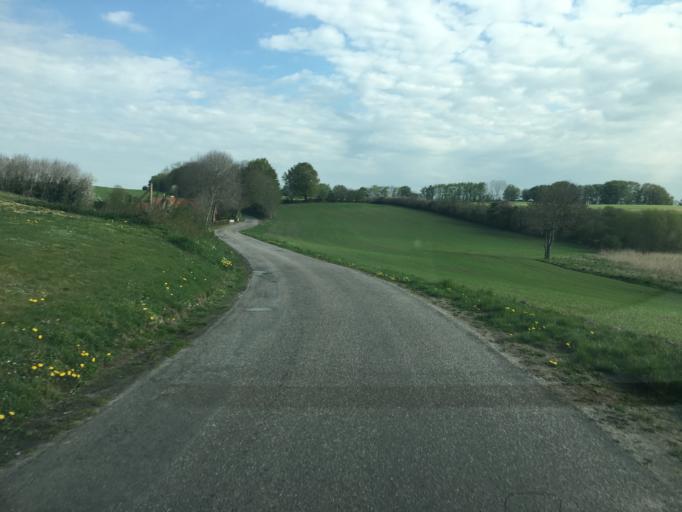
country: DK
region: South Denmark
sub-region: Haderslev Kommune
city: Vojens
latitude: 55.1911
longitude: 9.3901
